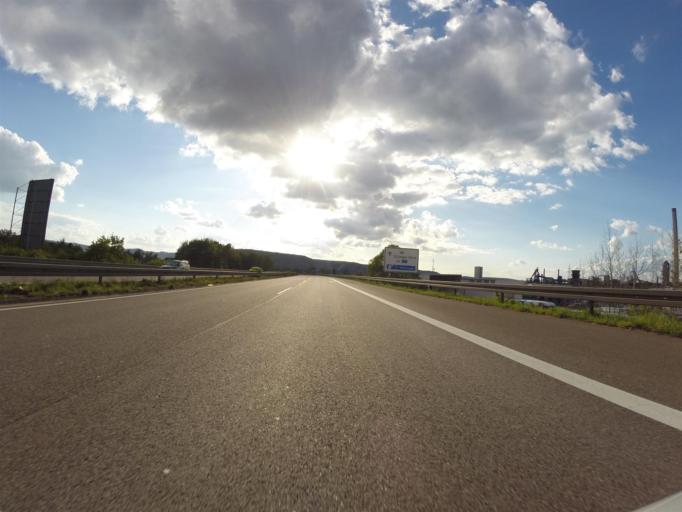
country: DE
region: Saarland
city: Dillingen
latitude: 49.3422
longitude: 6.7477
